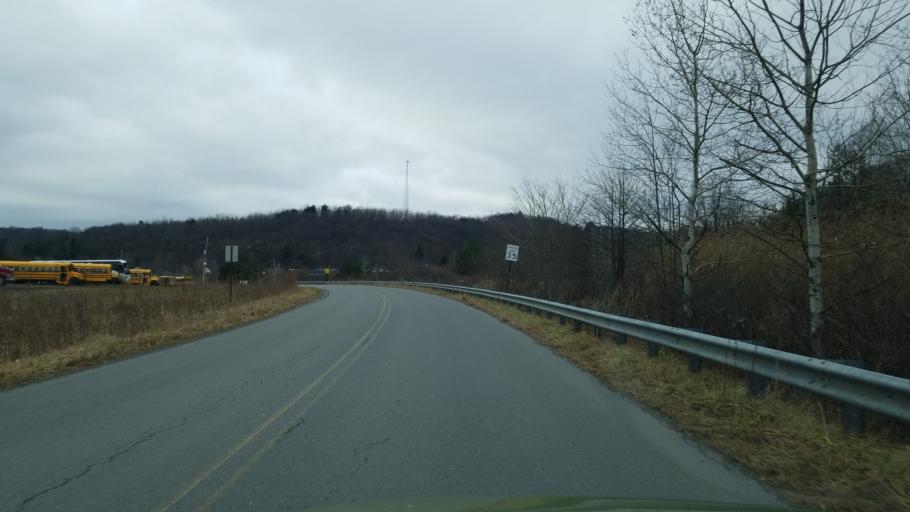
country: US
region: Pennsylvania
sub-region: Clearfield County
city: Clearfield
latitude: 41.0359
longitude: -78.4343
